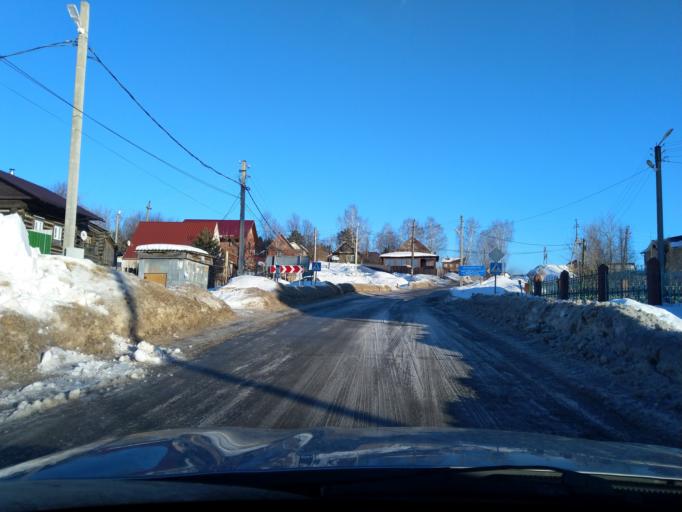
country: RU
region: Perm
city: Polazna
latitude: 58.3079
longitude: 56.4210
